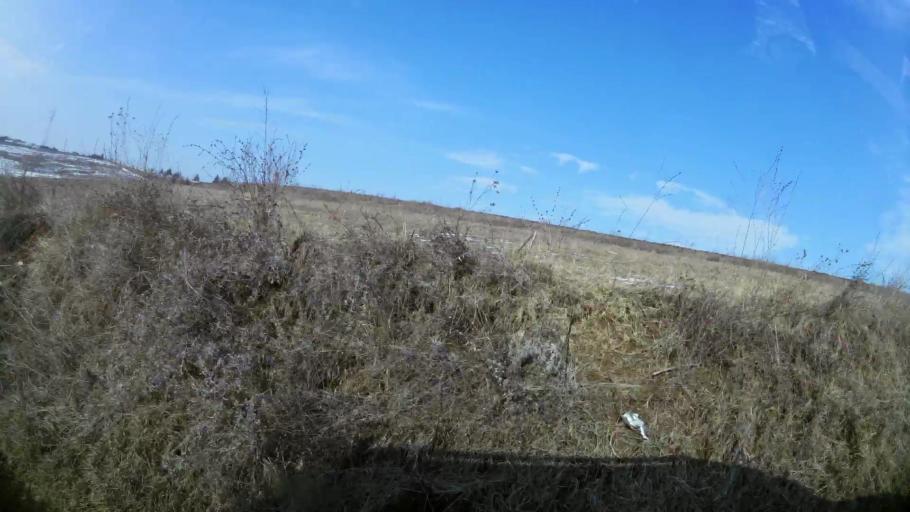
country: MK
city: Creshevo
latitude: 42.0172
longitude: 21.4964
